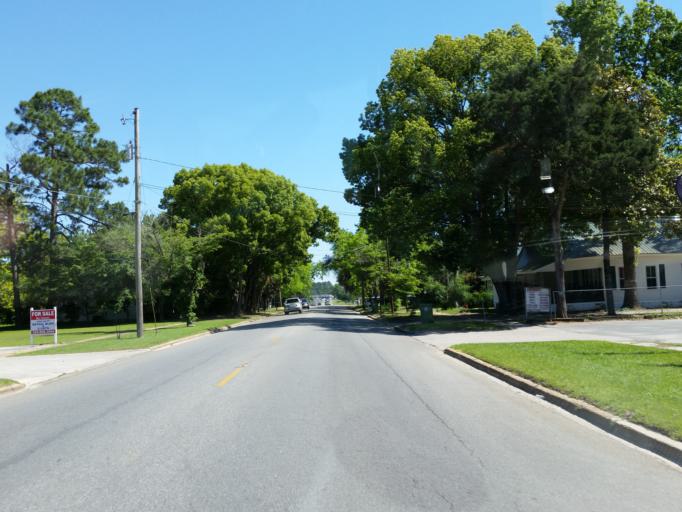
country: US
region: Georgia
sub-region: Cook County
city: Adel
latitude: 31.1308
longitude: -83.4212
